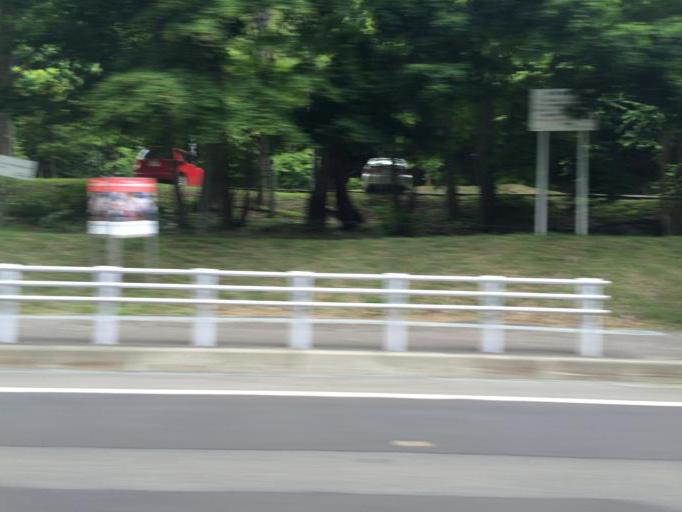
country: JP
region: Hokkaido
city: Sapporo
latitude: 43.0497
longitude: 141.2949
